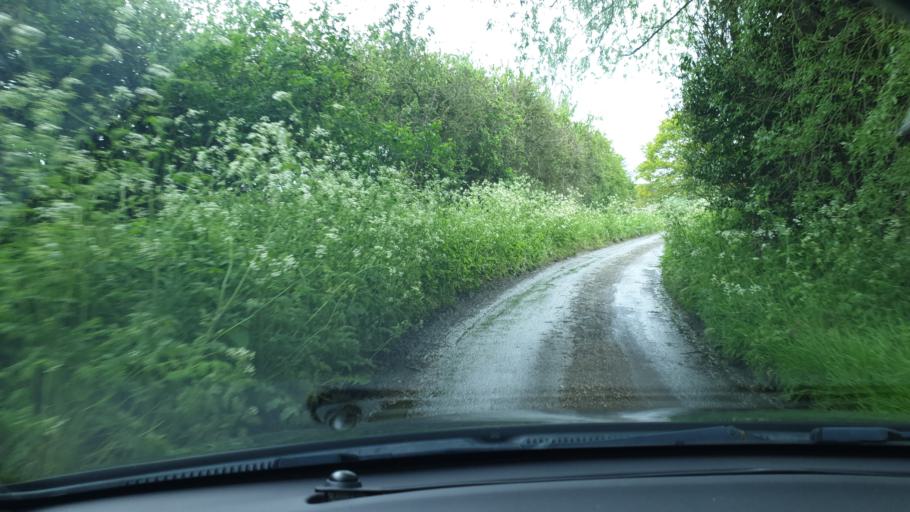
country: GB
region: England
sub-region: Essex
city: Dovercourt
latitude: 51.9104
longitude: 1.1982
